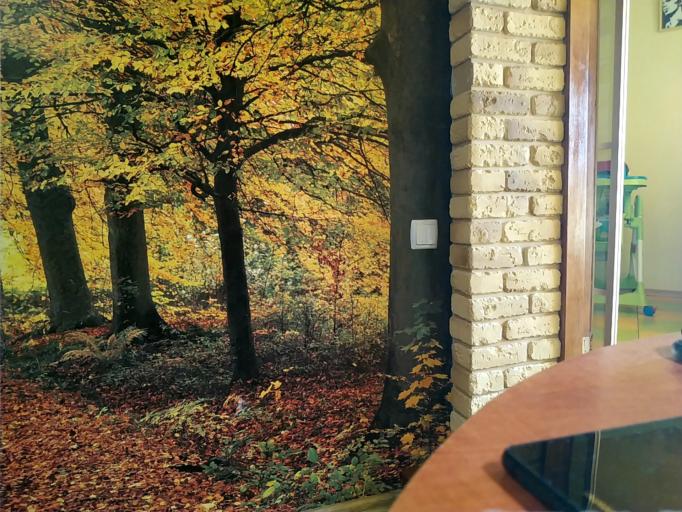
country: RU
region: Kaluga
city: Medyn'
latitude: 54.9538
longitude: 35.8794
